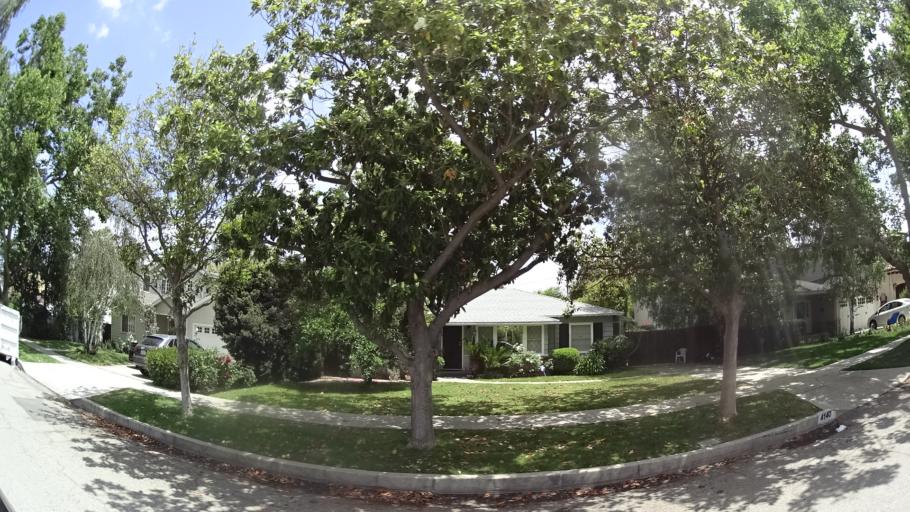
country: US
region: California
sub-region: Los Angeles County
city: Sherman Oaks
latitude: 34.1456
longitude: -118.4272
